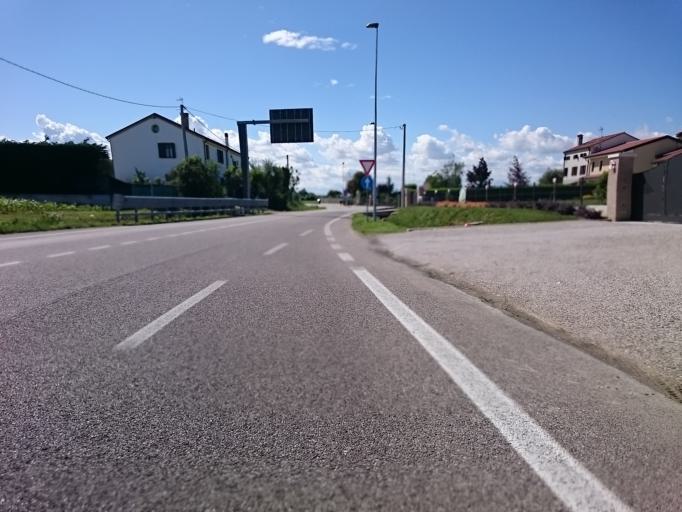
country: IT
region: Veneto
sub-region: Provincia di Venezia
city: Campolongo Maggiore Liettoli
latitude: 45.3472
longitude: 12.0137
